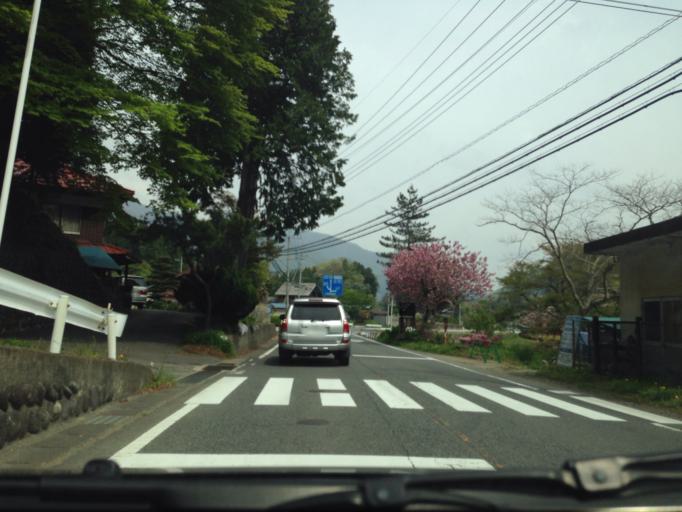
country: JP
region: Tochigi
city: Yaita
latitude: 36.9829
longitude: 139.7847
